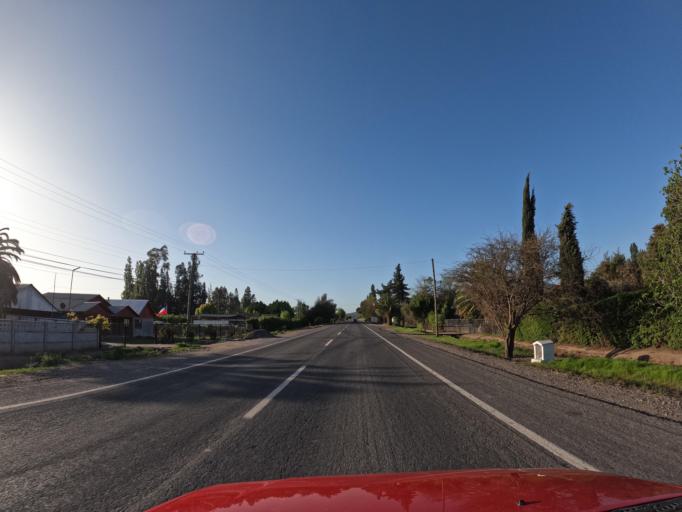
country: CL
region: O'Higgins
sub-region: Provincia de Colchagua
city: Santa Cruz
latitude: -34.4500
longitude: -71.3658
